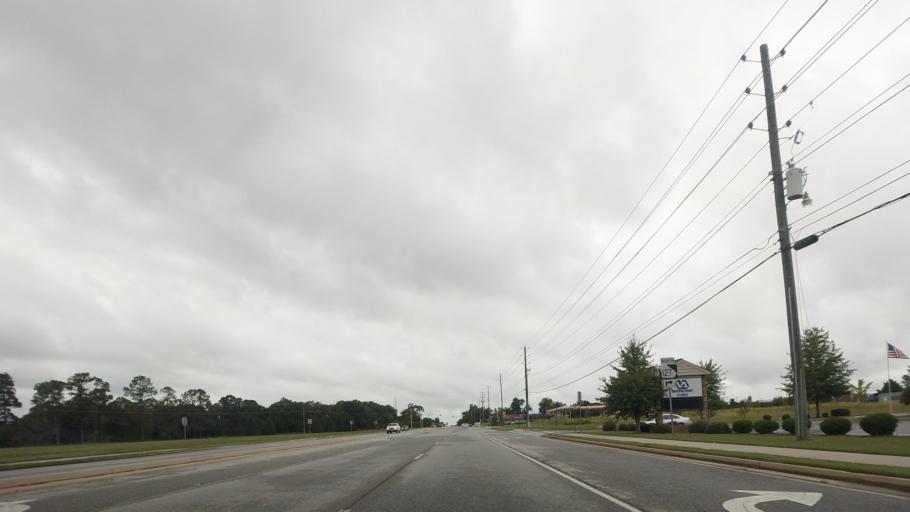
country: US
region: Georgia
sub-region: Houston County
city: Perry
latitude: 32.5034
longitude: -83.6626
